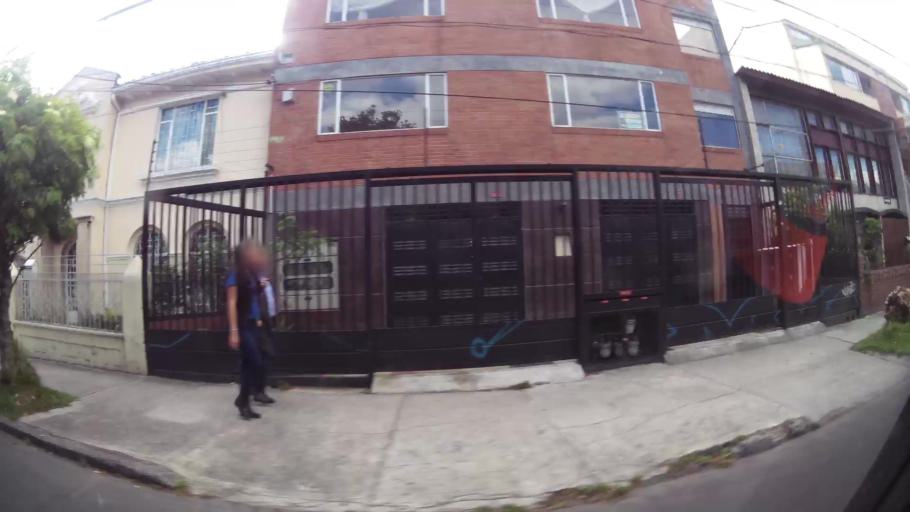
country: CO
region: Bogota D.C.
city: Bogota
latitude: 4.6423
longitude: -74.0681
